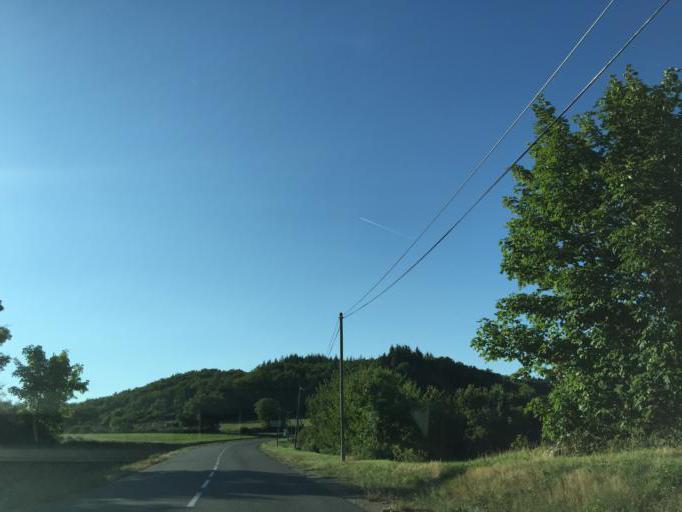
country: FR
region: Midi-Pyrenees
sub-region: Departement de l'Aveyron
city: Saint-Georges-de-Luzencon
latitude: 44.0912
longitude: 2.9018
